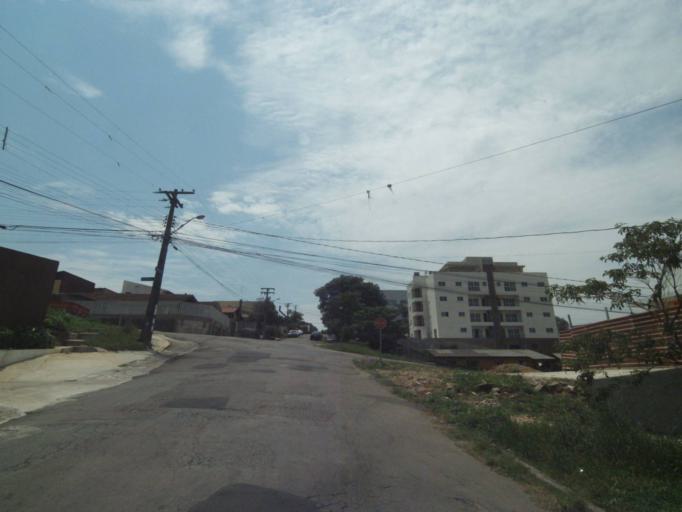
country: BR
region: Parana
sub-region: Pinhais
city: Pinhais
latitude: -25.3981
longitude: -49.2095
